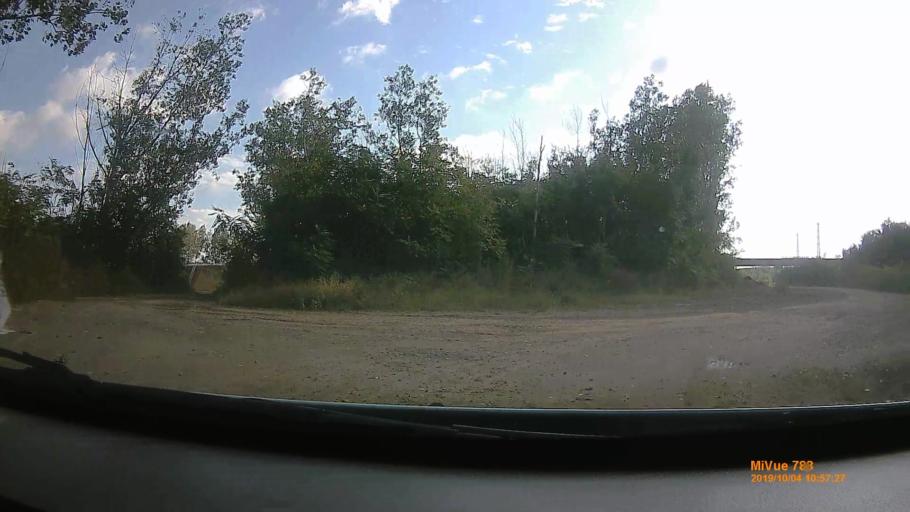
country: HU
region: Szabolcs-Szatmar-Bereg
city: Nyirtelek
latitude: 47.9810
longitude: 21.6635
